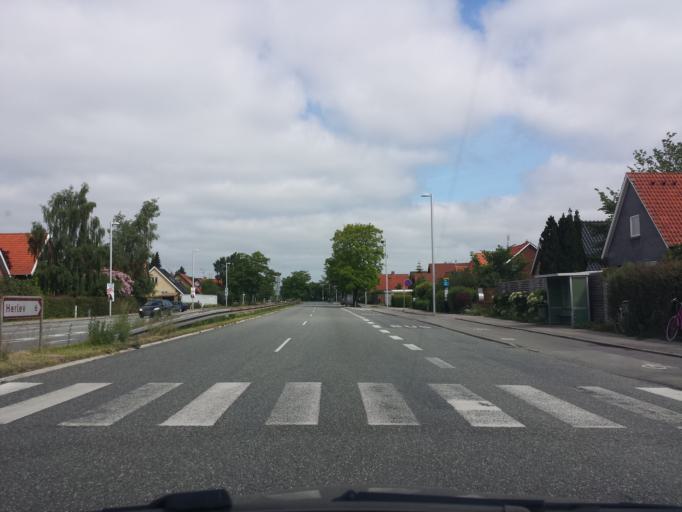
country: DK
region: Capital Region
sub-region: Glostrup Kommune
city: Glostrup
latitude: 55.6748
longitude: 12.3956
